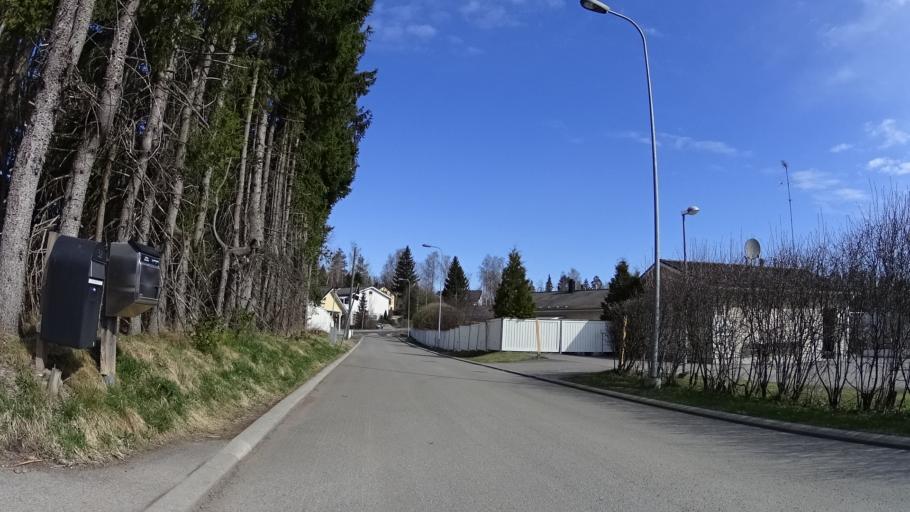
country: FI
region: Uusimaa
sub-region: Helsinki
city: Kilo
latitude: 60.2408
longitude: 24.7808
